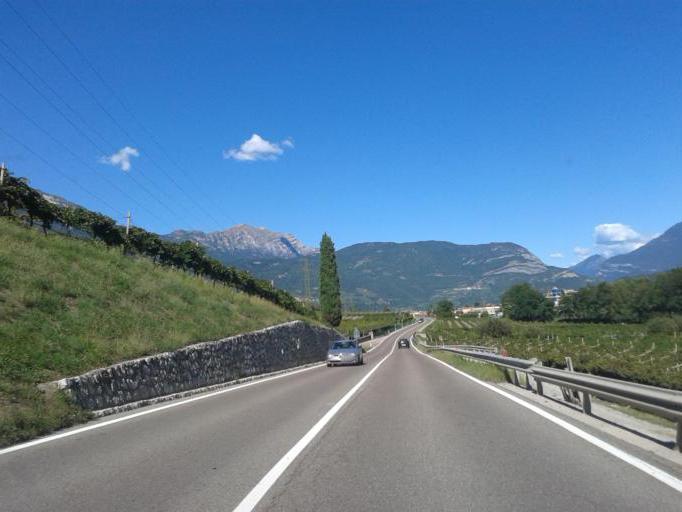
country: IT
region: Trentino-Alto Adige
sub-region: Provincia di Trento
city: Isera
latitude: 45.8744
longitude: 11.0060
